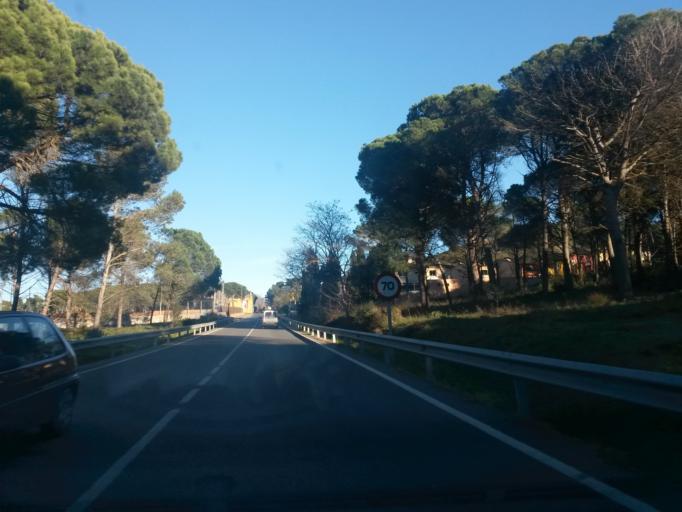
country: ES
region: Catalonia
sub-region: Provincia de Girona
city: Begur
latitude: 41.9524
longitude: 3.1962
